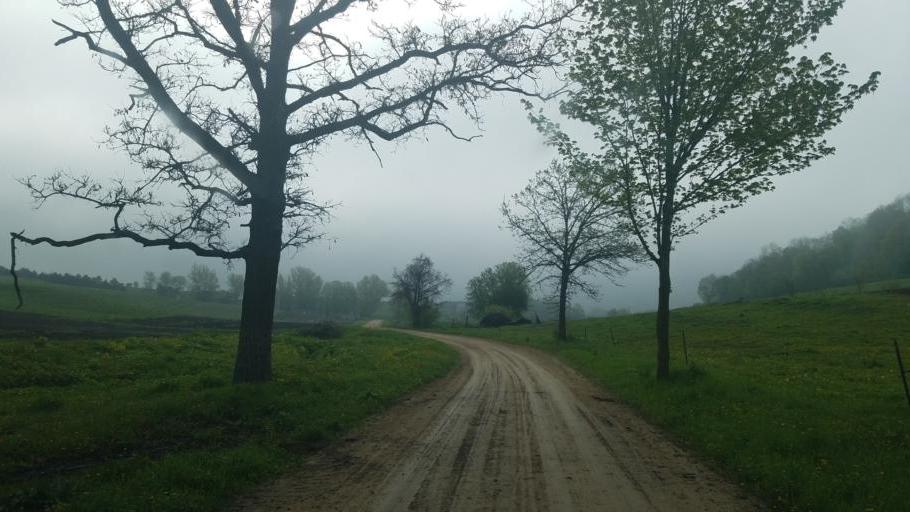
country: US
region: Wisconsin
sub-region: Vernon County
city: Hillsboro
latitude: 43.6241
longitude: -90.3930
